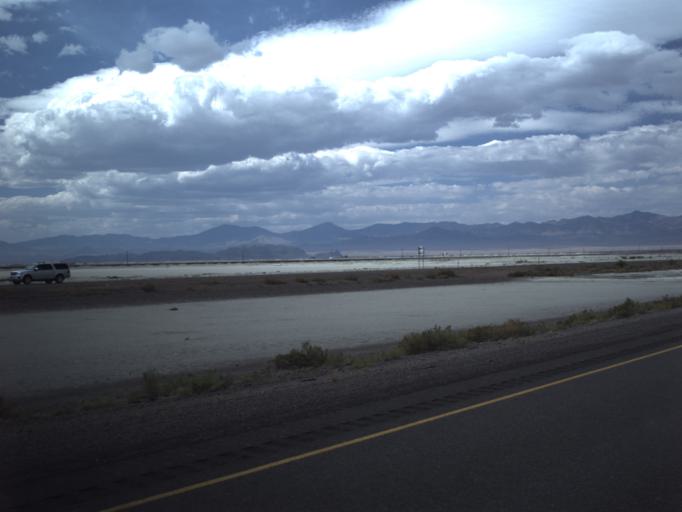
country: US
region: Utah
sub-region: Tooele County
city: Wendover
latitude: 40.7414
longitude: -113.9535
